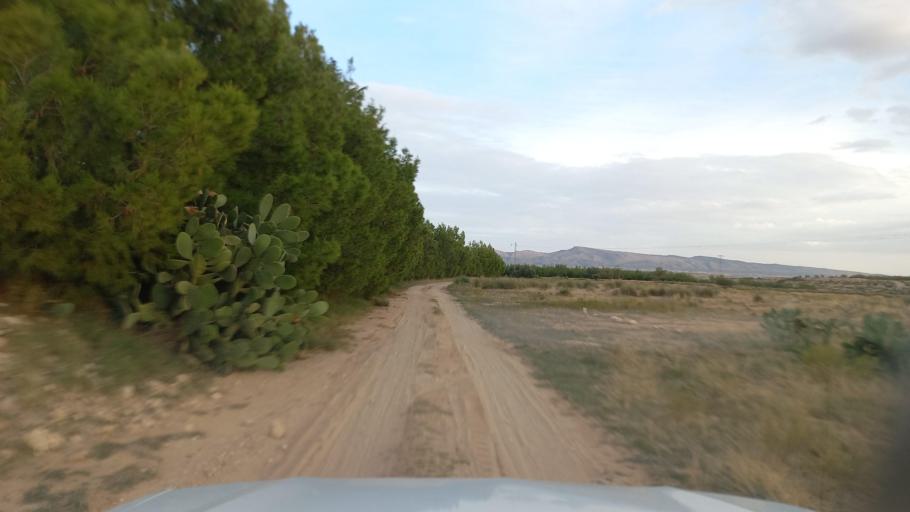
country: TN
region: Al Qasrayn
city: Sbiba
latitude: 35.4246
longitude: 9.0971
